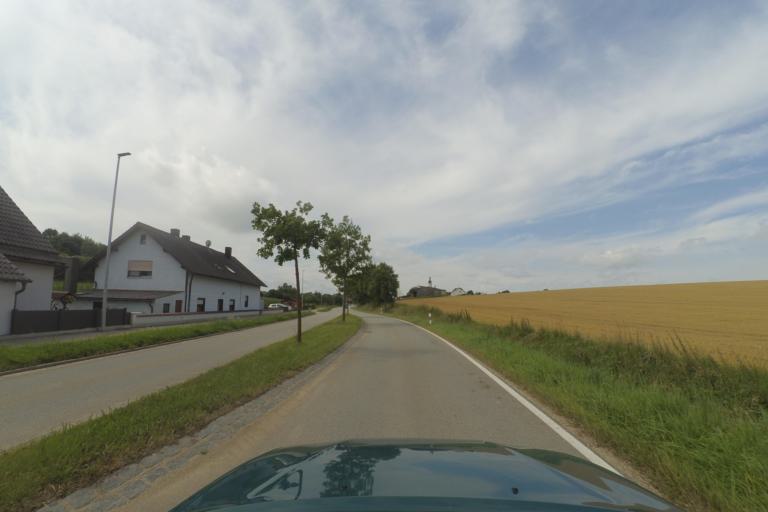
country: DE
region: Bavaria
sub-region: Upper Palatinate
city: Thalmassing
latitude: 48.9153
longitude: 12.1647
